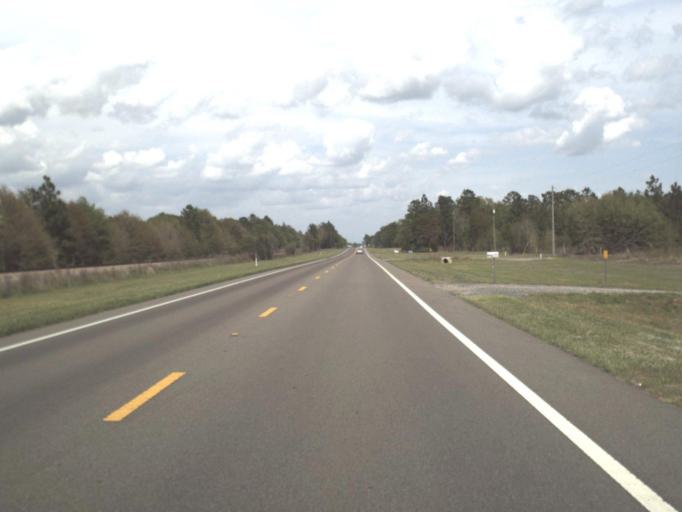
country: US
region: Florida
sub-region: Santa Rosa County
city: East Milton
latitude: 30.6947
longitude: -86.8036
